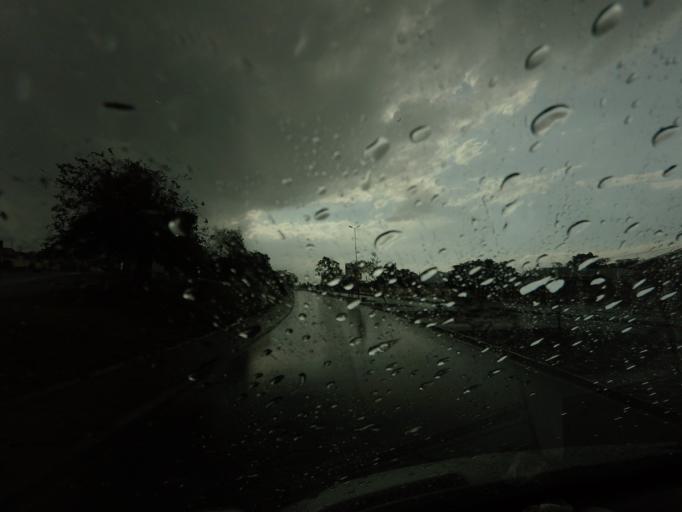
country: SZ
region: Manzini
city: Manzini
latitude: -26.4981
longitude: 31.3704
